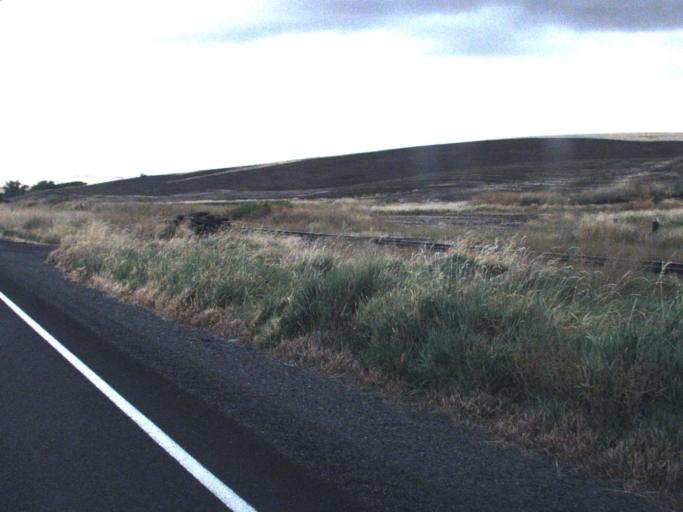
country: US
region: Washington
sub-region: Whitman County
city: Colfax
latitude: 47.1972
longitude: -117.3441
